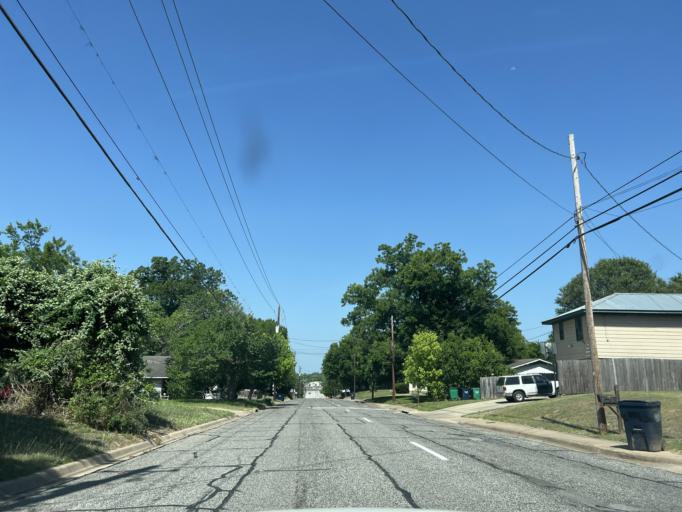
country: US
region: Texas
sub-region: Washington County
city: Brenham
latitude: 30.1690
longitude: -96.3872
